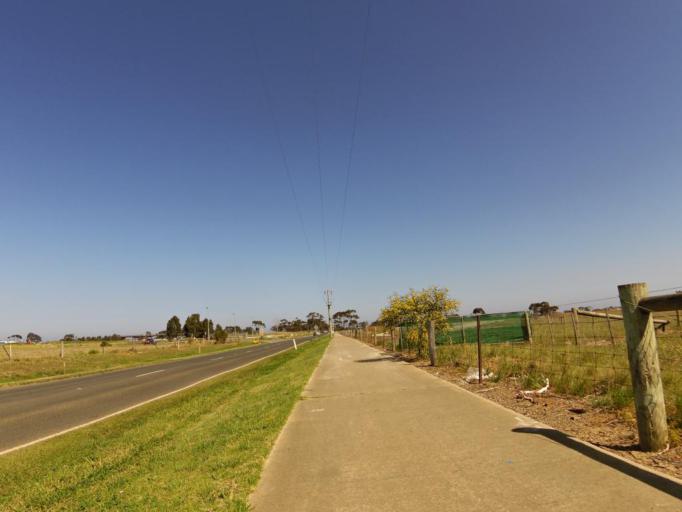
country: AU
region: Victoria
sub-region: Wyndham
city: Hoppers Crossing
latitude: -37.8953
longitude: 144.7011
